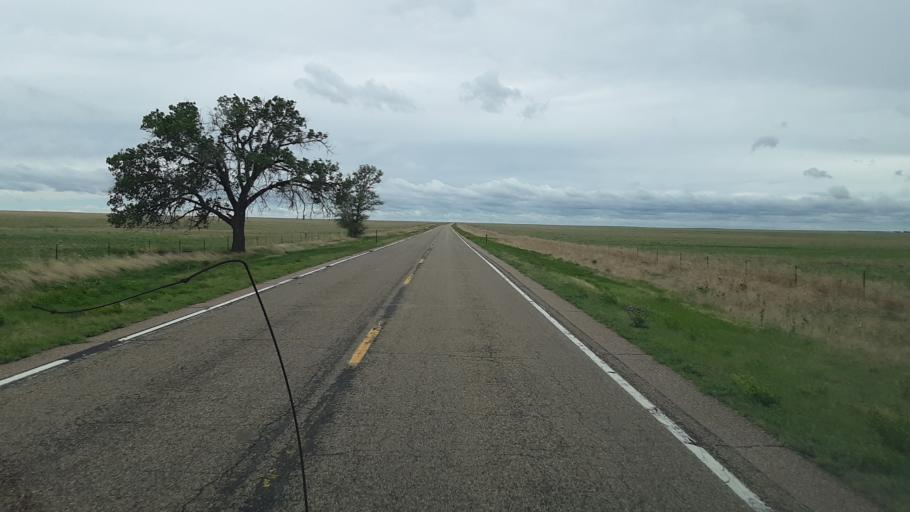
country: US
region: Colorado
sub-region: Lincoln County
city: Hugo
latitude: 38.8521
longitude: -103.7322
